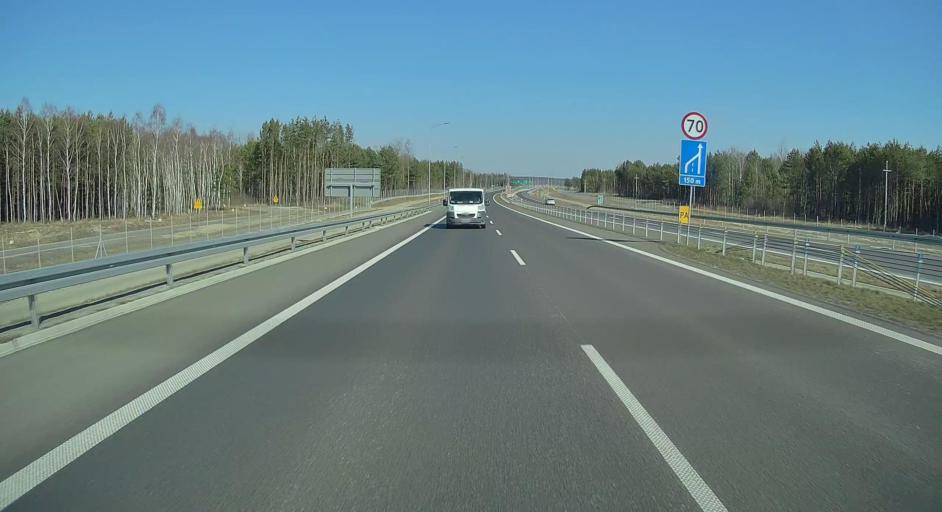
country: PL
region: Subcarpathian Voivodeship
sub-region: Powiat nizanski
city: Przedzel
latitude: 50.4887
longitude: 22.1910
